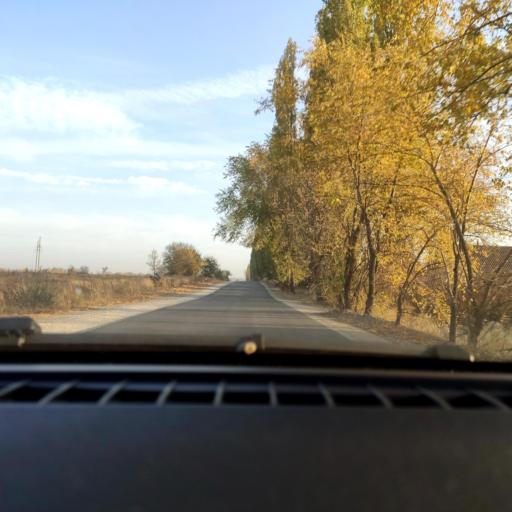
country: RU
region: Voronezj
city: Maslovka
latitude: 51.5198
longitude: 39.2248
